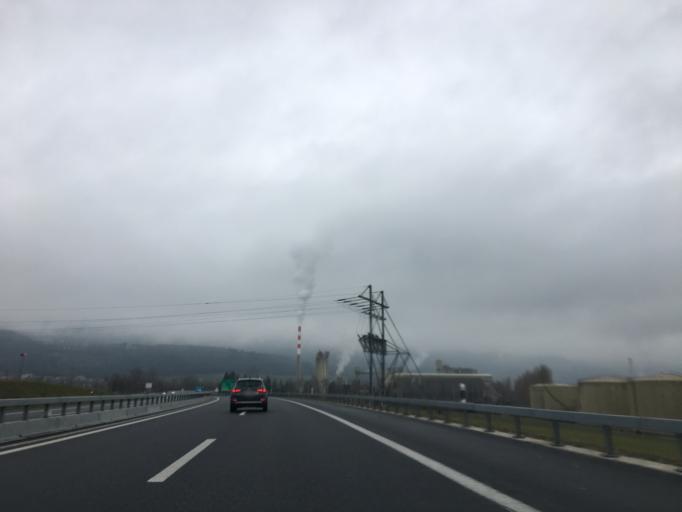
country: CH
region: Neuchatel
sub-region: Neuchatel District
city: Cornaux
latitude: 47.0278
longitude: 7.0291
